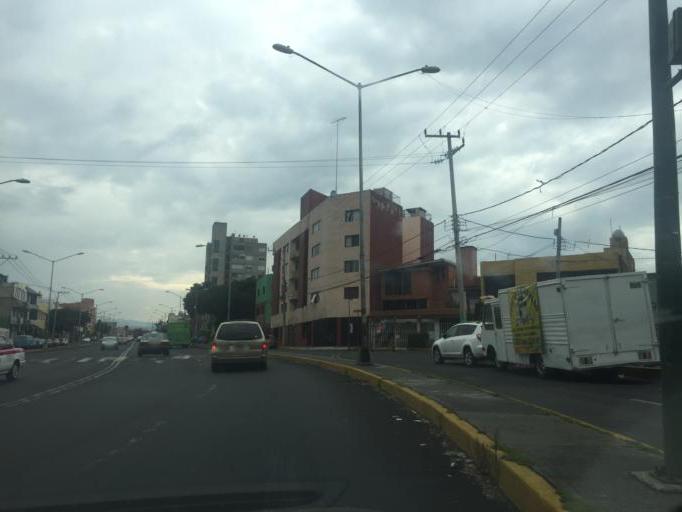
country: MX
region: Mexico City
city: Alvaro Obregon
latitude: 19.3692
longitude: -99.2244
